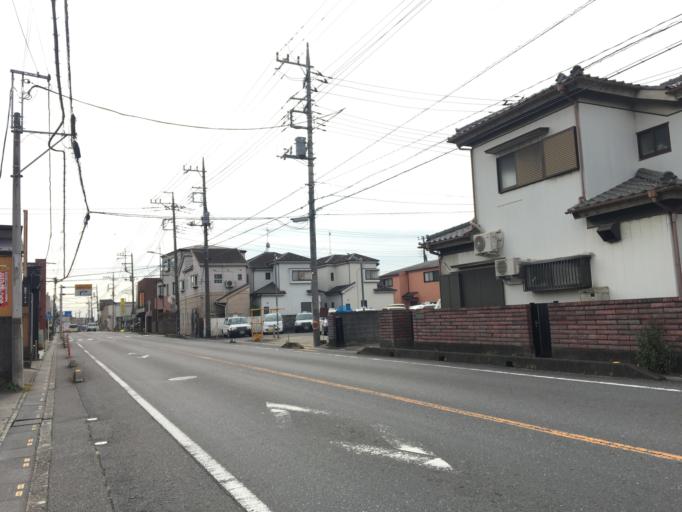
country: JP
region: Saitama
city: Yoshikawa
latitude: 35.8882
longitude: 139.8408
